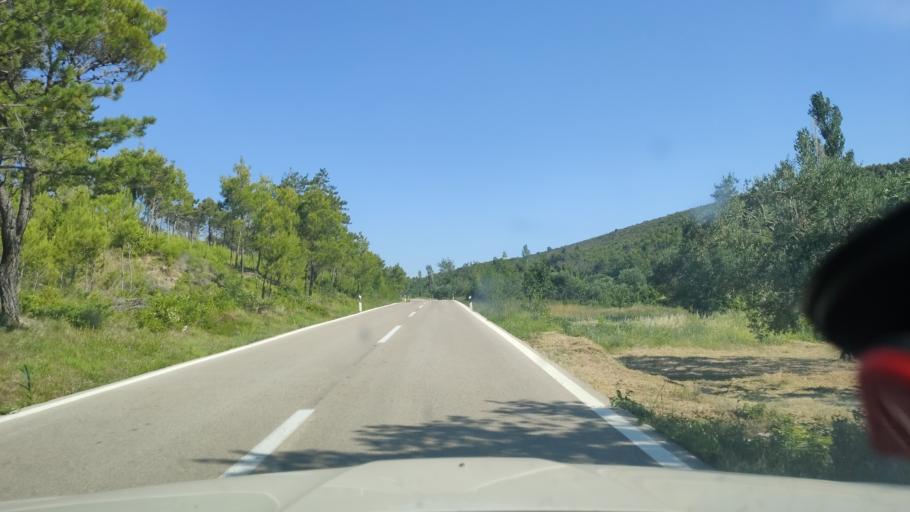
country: HR
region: Sibensko-Kniniska
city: Zaton
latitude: 43.8605
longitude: 15.8925
